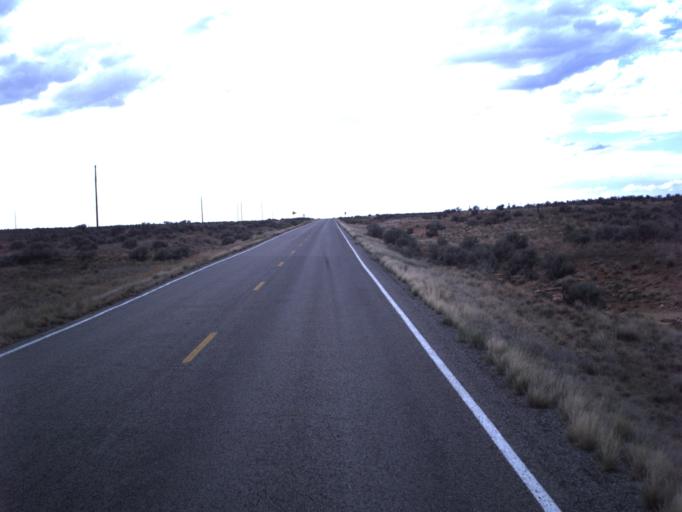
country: US
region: Utah
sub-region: San Juan County
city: Blanding
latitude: 37.4276
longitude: -109.3542
